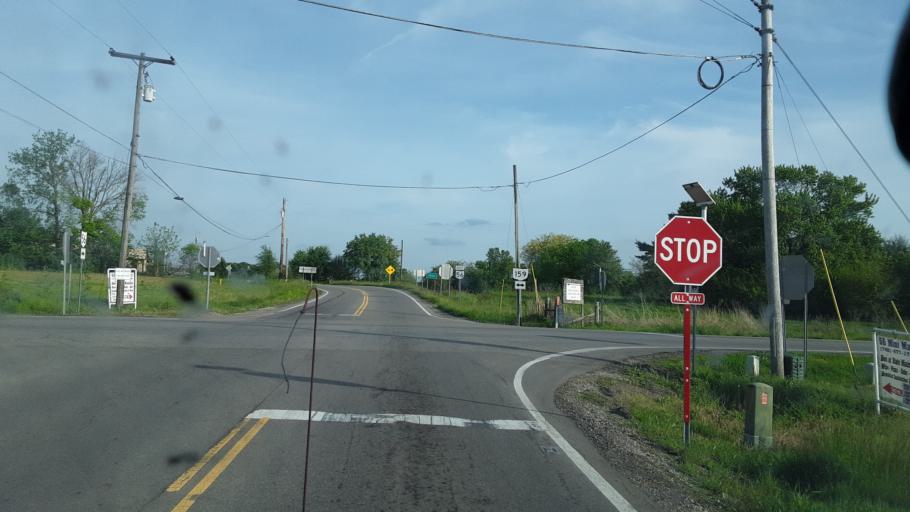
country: US
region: Ohio
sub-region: Ross County
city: Kingston
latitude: 39.5328
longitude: -82.8413
